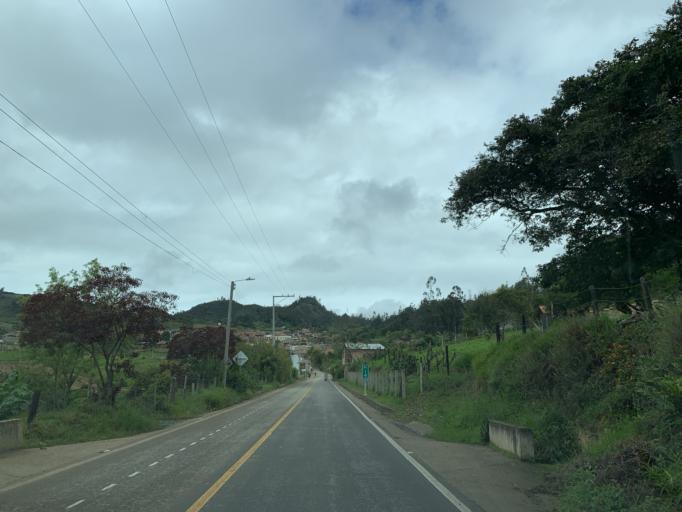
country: CO
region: Boyaca
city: Tibana
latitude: 5.3226
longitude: -73.3944
